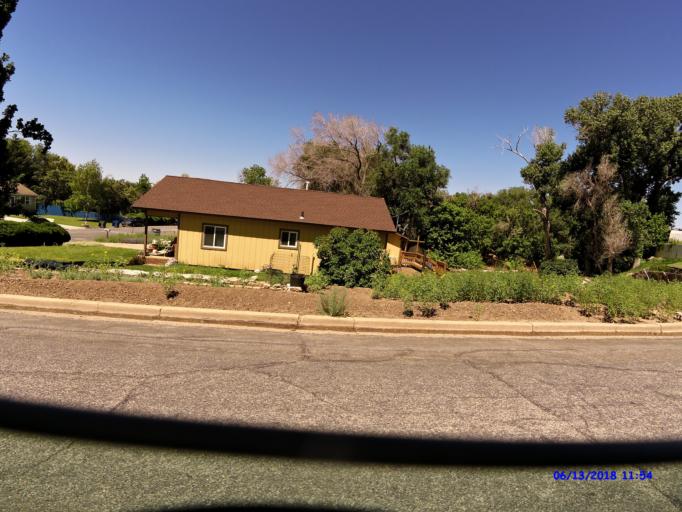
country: US
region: Utah
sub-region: Weber County
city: Ogden
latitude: 41.2278
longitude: -111.9453
